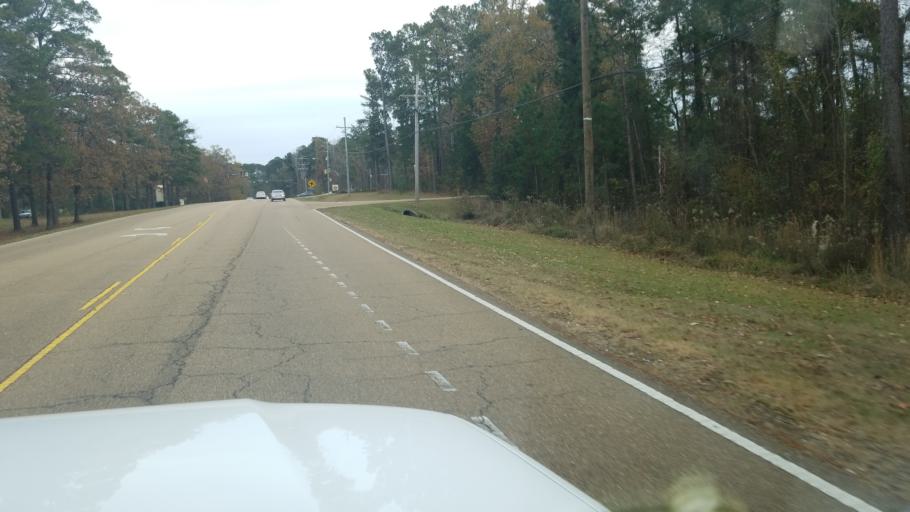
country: US
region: Mississippi
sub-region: Rankin County
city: Brandon
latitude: 32.3733
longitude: -90.0191
